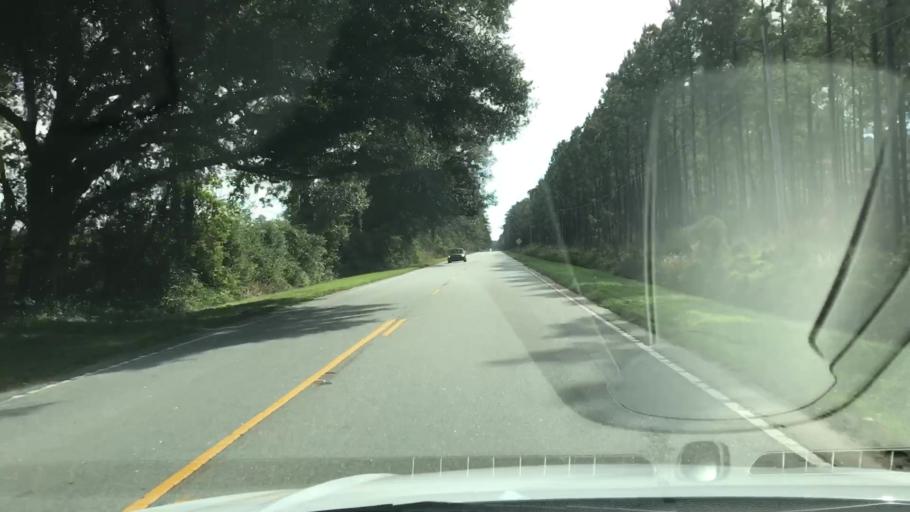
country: US
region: South Carolina
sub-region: Colleton County
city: Walterboro
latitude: 32.7943
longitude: -80.4861
